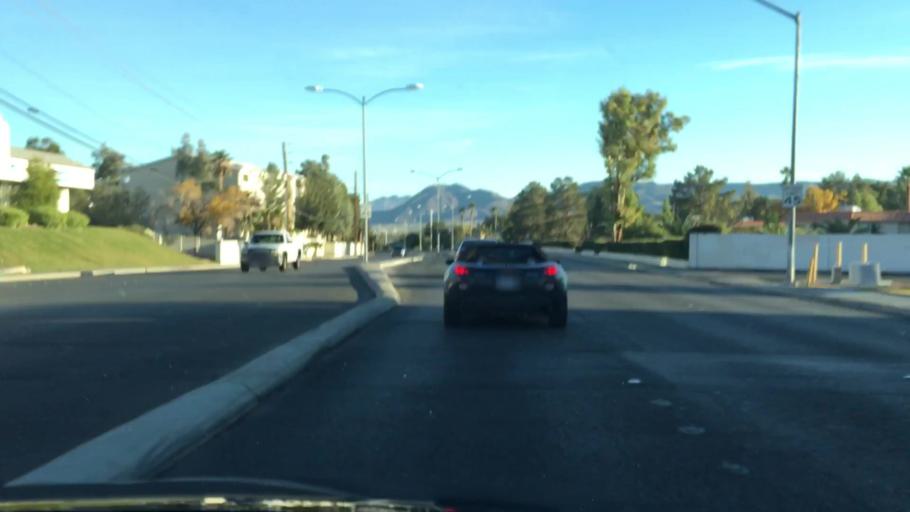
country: US
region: Nevada
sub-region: Clark County
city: Whitney
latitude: 36.0676
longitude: -115.0678
